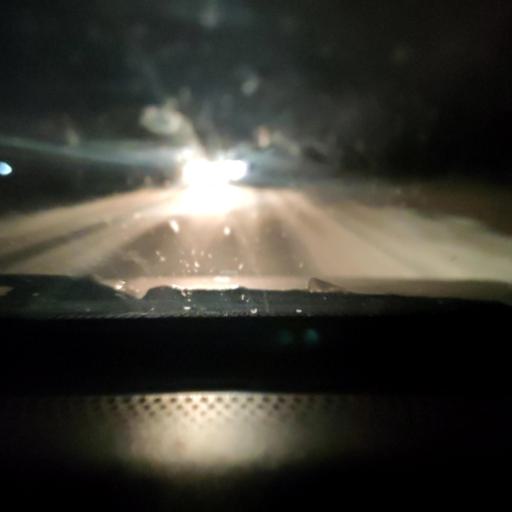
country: RU
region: Perm
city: Kondratovo
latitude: 57.9251
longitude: 56.0662
